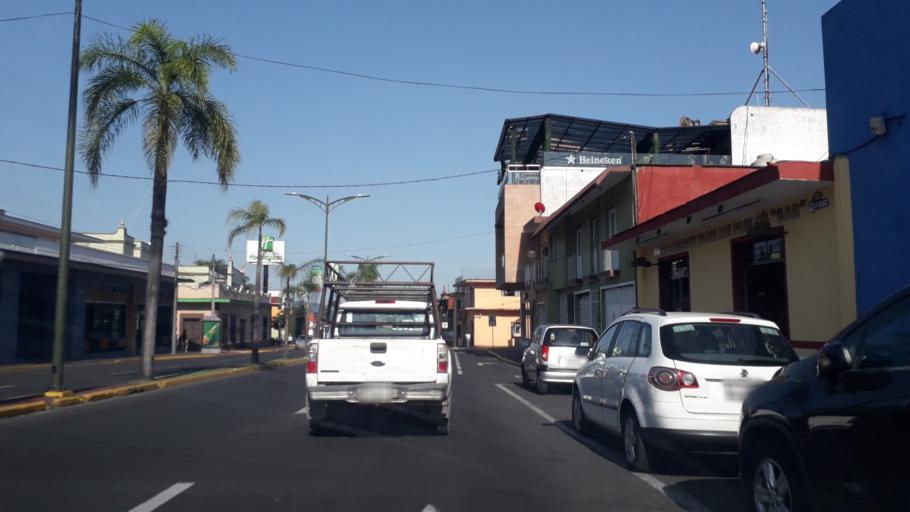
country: MX
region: Veracruz
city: Orizaba
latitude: 18.8475
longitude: -97.0974
